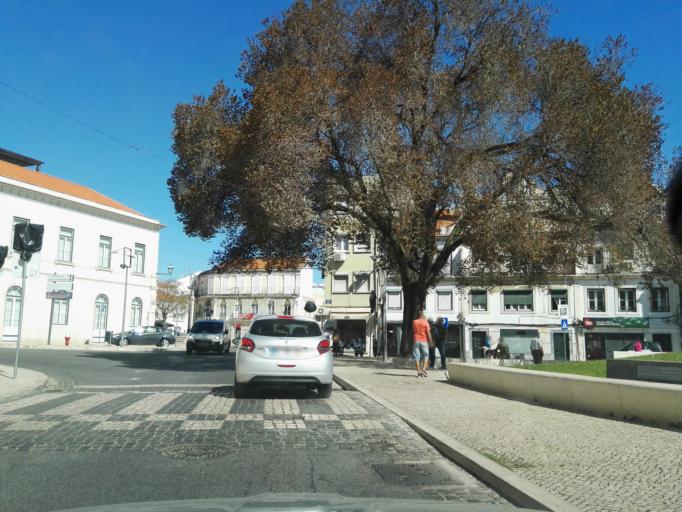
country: PT
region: Lisbon
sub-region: Vila Franca de Xira
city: Vila Franca de Xira
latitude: 38.9536
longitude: -8.9897
